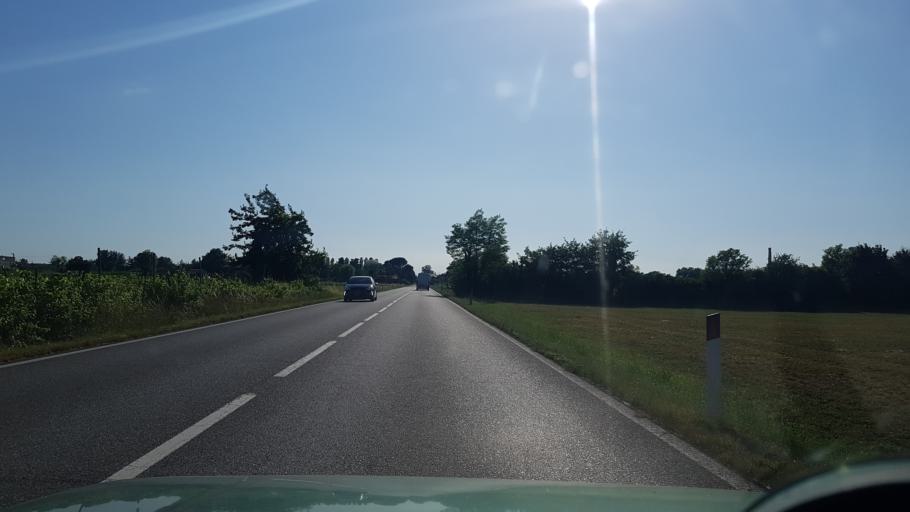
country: IT
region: Friuli Venezia Giulia
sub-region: Provincia di Udine
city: Ruda
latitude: 45.8388
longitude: 13.3849
